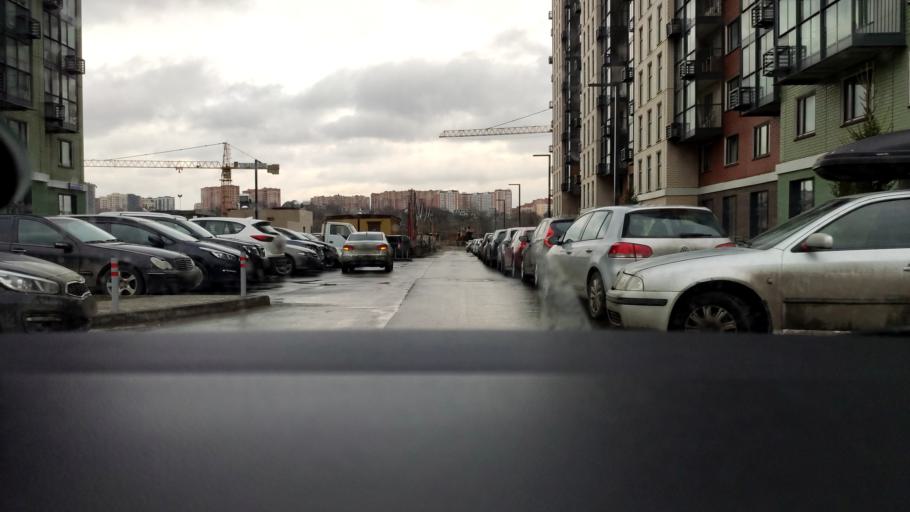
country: RU
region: Moskovskaya
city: Pavshino
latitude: 55.8600
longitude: 37.3720
